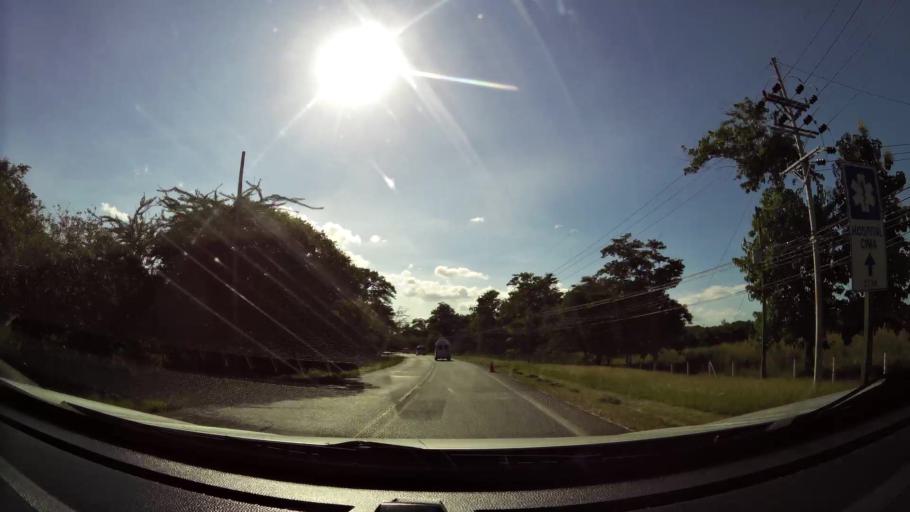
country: CR
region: Guanacaste
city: Sardinal
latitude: 10.5794
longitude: -85.5778
